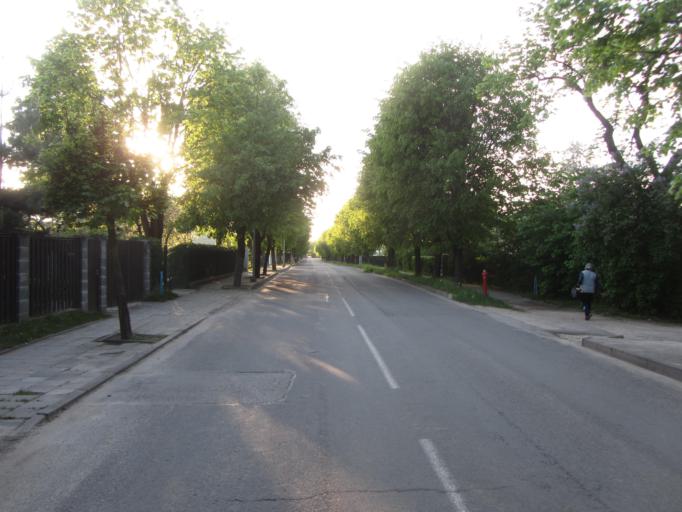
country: LT
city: Sirvintos
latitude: 55.0348
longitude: 24.9714
